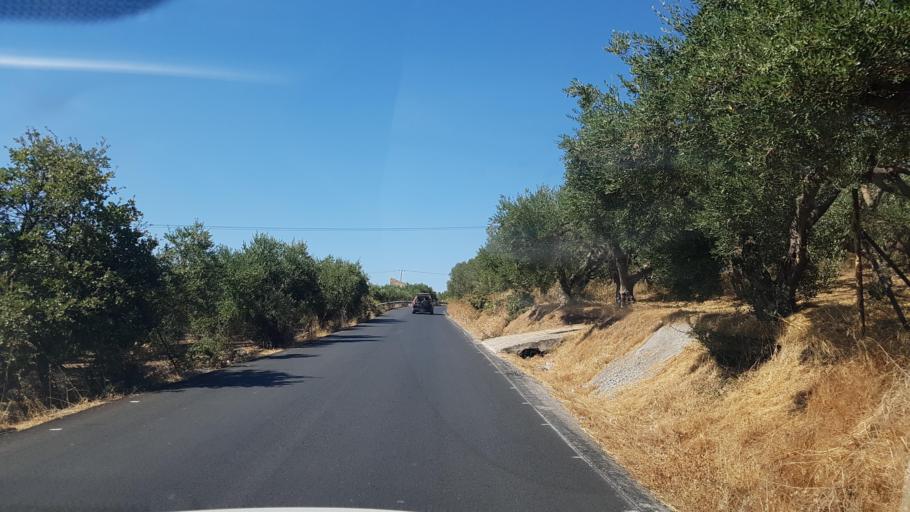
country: GR
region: Crete
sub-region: Nomos Chanias
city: Kissamos
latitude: 35.4892
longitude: 23.6916
